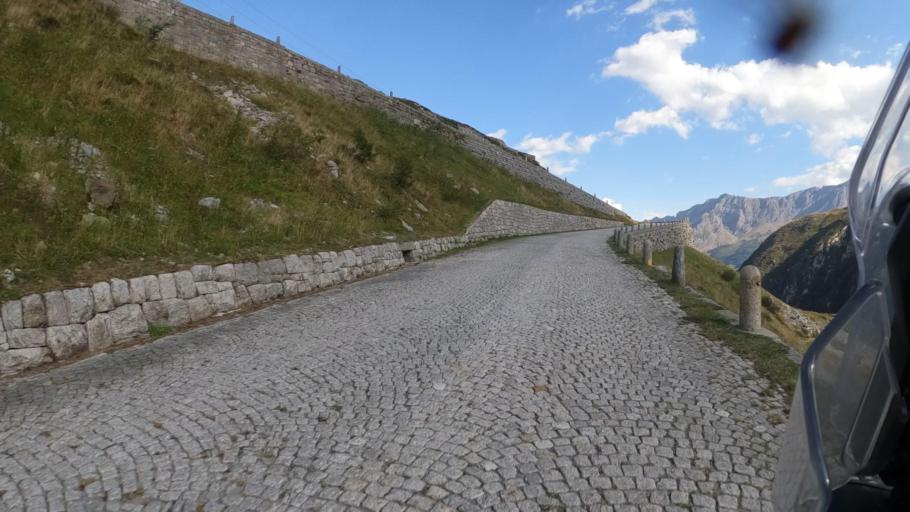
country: CH
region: Ticino
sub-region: Leventina District
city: Airolo
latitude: 46.5472
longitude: 8.5687
